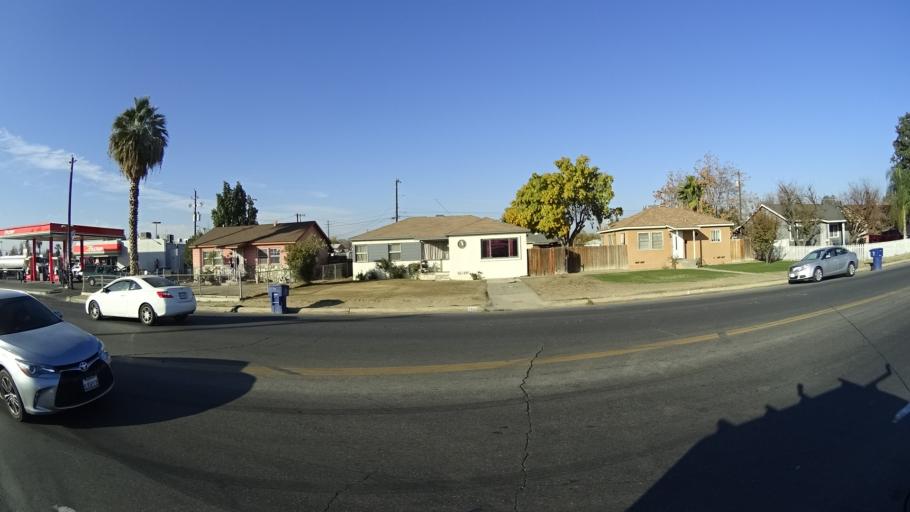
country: US
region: California
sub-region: Kern County
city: Bakersfield
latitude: 35.3394
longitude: -119.0177
